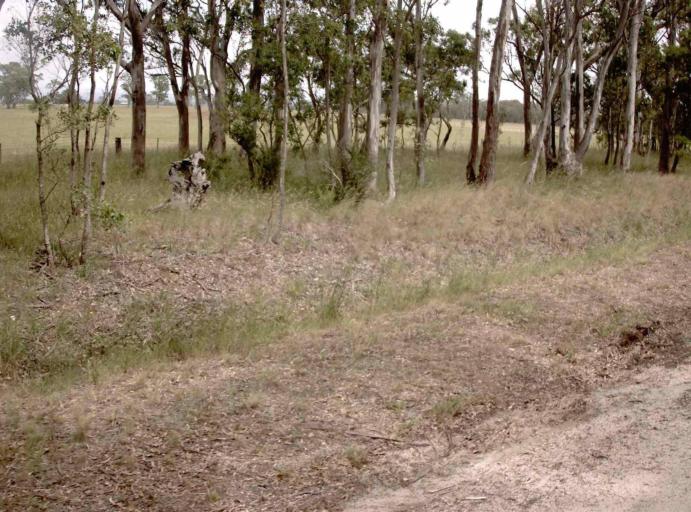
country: AU
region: Victoria
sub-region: Wellington
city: Sale
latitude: -37.9054
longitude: 147.0770
